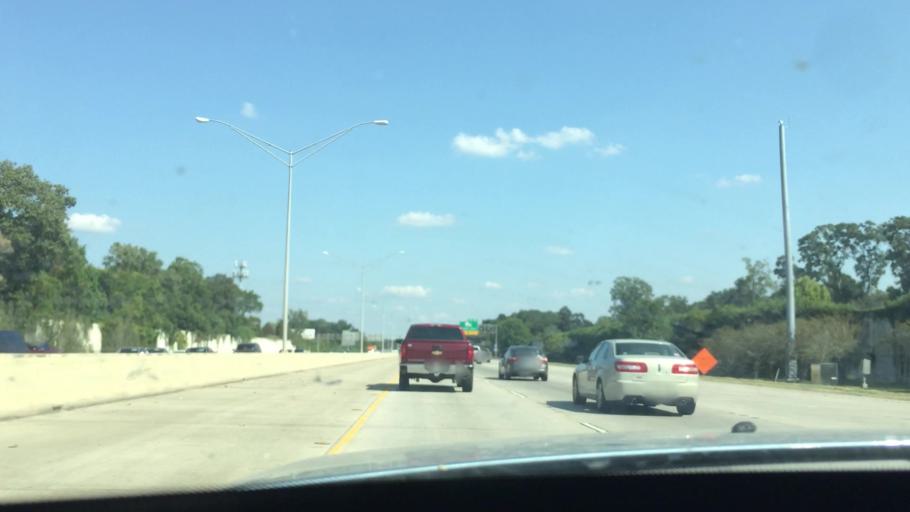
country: US
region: Louisiana
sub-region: East Baton Rouge Parish
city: Westminster
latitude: 30.4181
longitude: -91.1075
